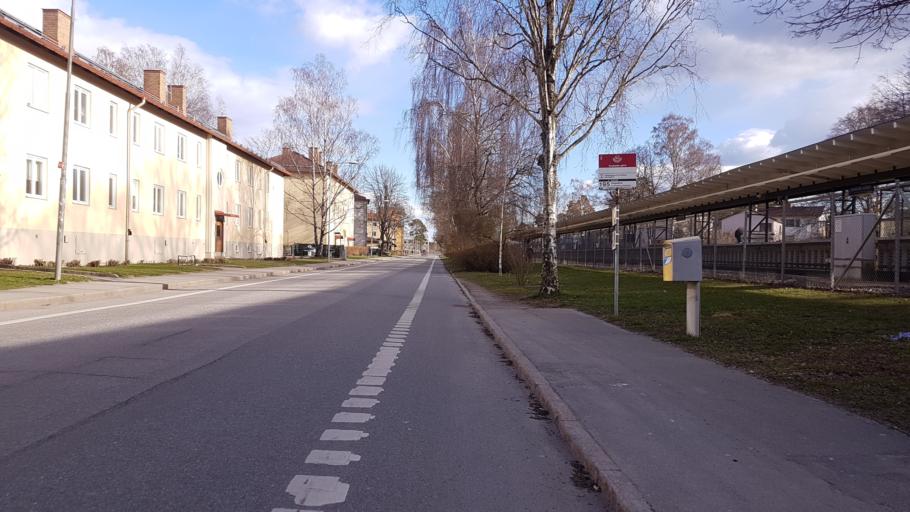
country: SE
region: Stockholm
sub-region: Stockholms Kommun
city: Arsta
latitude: 59.2894
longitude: 18.0704
